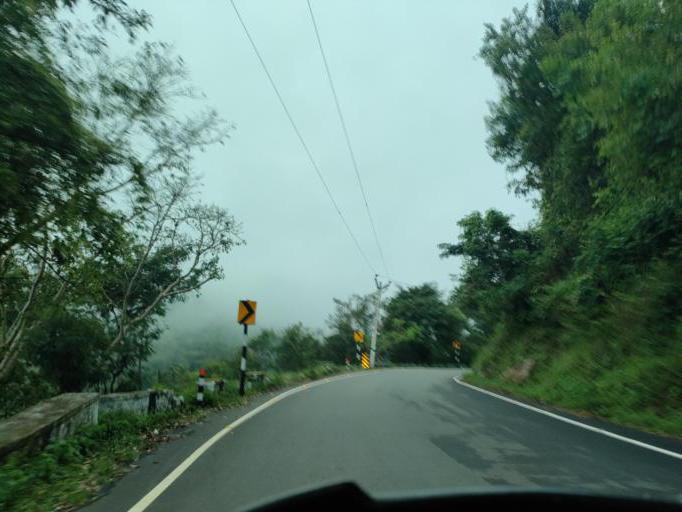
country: IN
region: Tamil Nadu
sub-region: Dindigul
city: Ayakudi
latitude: 10.3581
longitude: 77.5561
